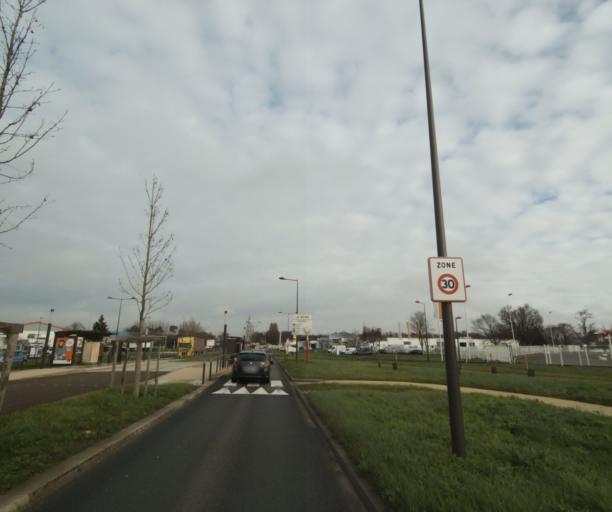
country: FR
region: Pays de la Loire
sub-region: Departement de la Sarthe
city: Allonnes
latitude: 47.9782
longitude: 0.1730
